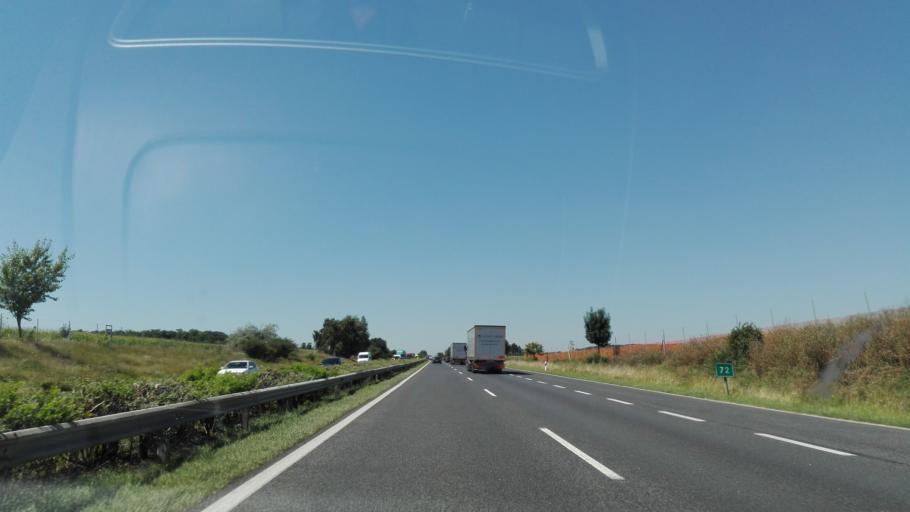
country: HU
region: Komarom-Esztergom
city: Kocs
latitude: 47.6326
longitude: 18.2496
